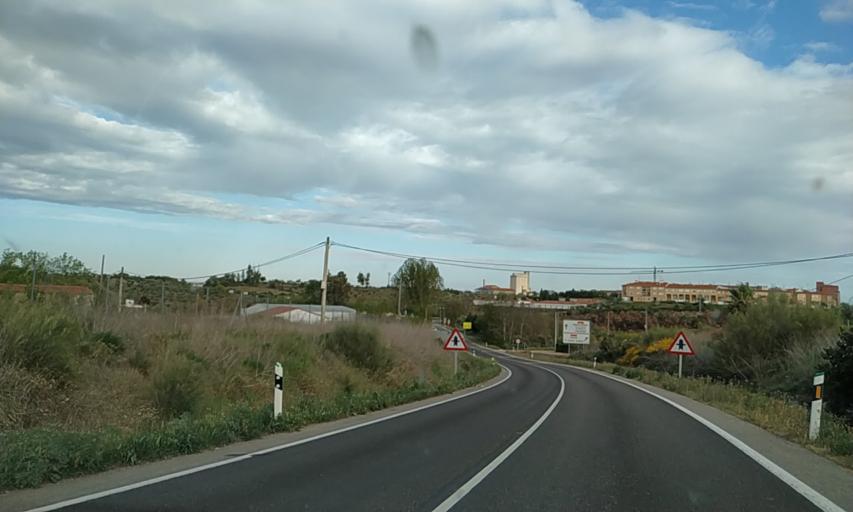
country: ES
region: Extremadura
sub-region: Provincia de Caceres
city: Coria
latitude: 39.9973
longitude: -6.5464
